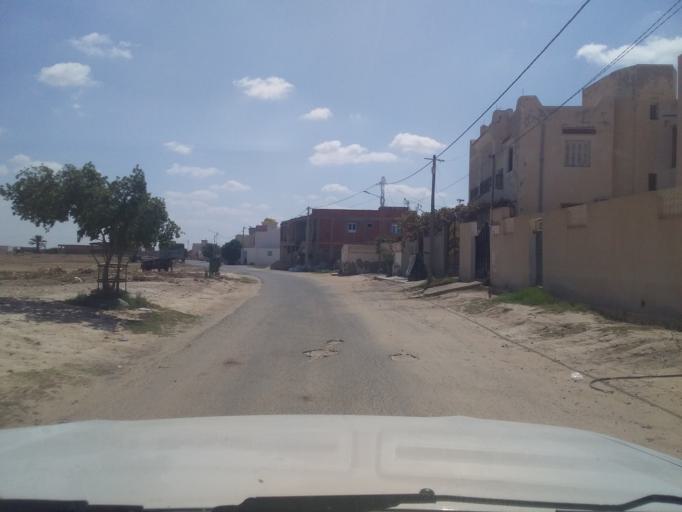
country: TN
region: Madanin
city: Medenine
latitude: 33.6142
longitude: 10.2971
